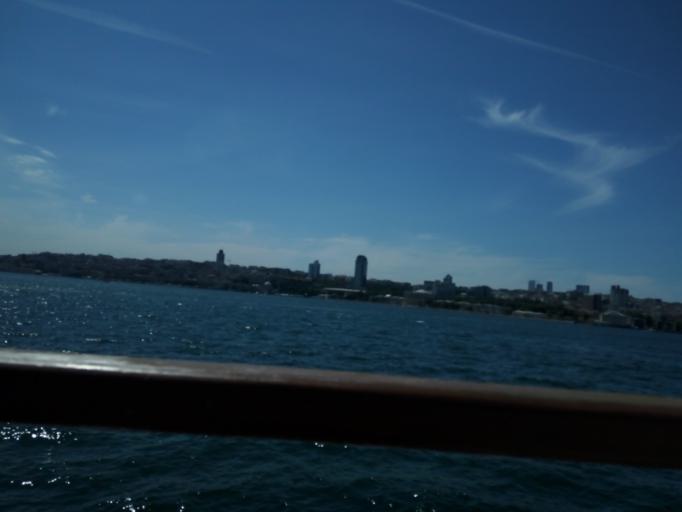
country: TR
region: Istanbul
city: UEskuedar
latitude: 41.0338
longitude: 29.0137
